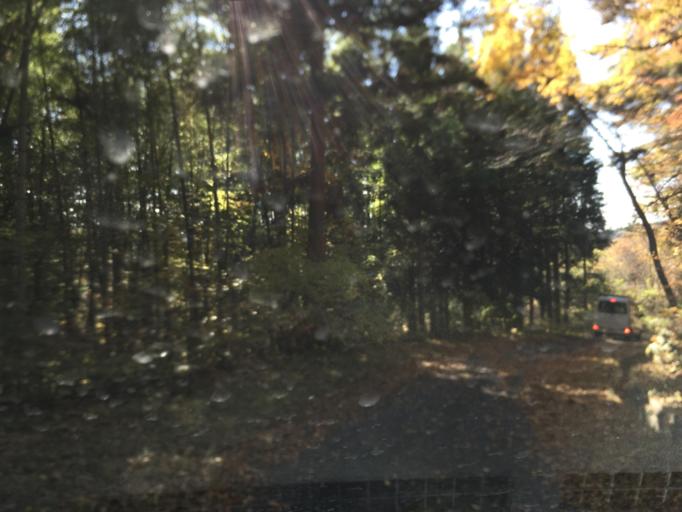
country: JP
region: Iwate
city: Ichinoseki
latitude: 38.9647
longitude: 141.4164
